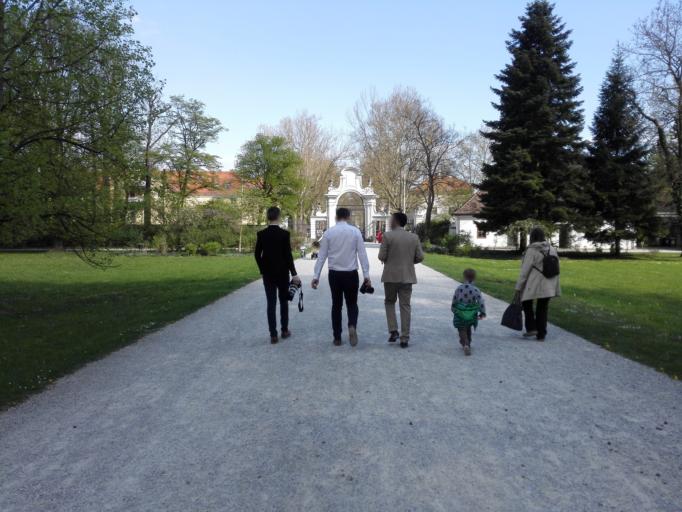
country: AT
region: Styria
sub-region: Graz Stadt
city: Wetzelsdorf
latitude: 47.0729
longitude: 15.3941
